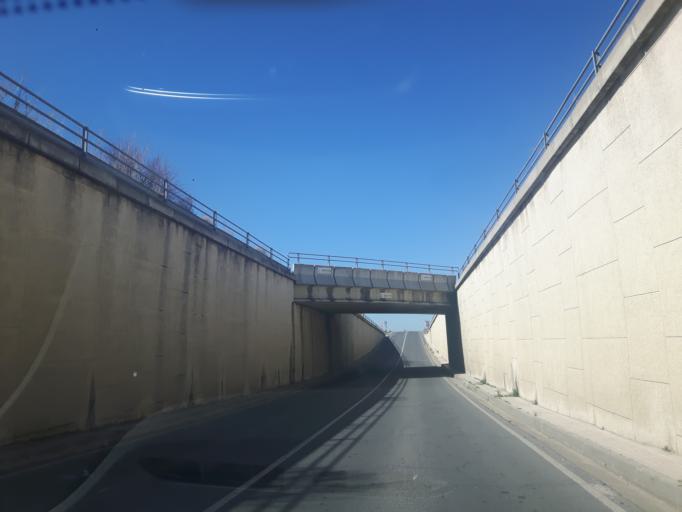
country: ES
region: Castille and Leon
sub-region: Provincia de Salamanca
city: Penaranda de Bracamonte
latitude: 40.8998
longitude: -5.2099
